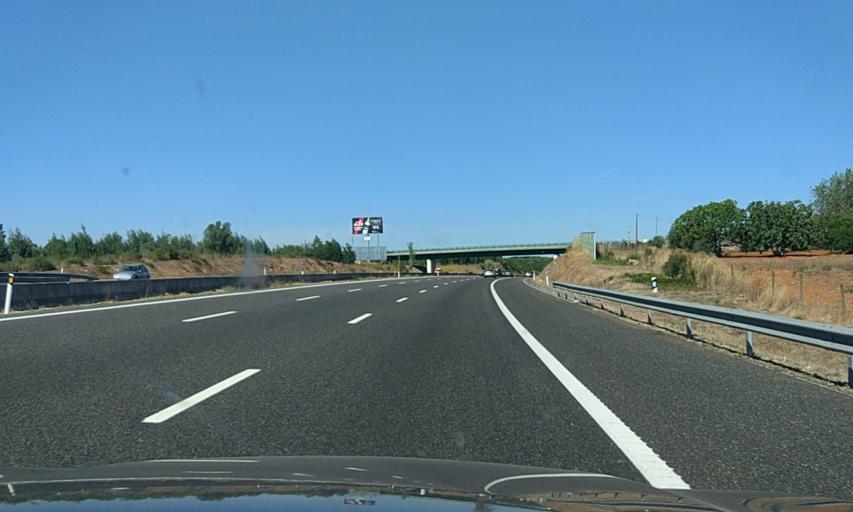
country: PT
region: Santarem
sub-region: Cartaxo
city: Cartaxo
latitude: 39.2316
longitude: -8.7633
